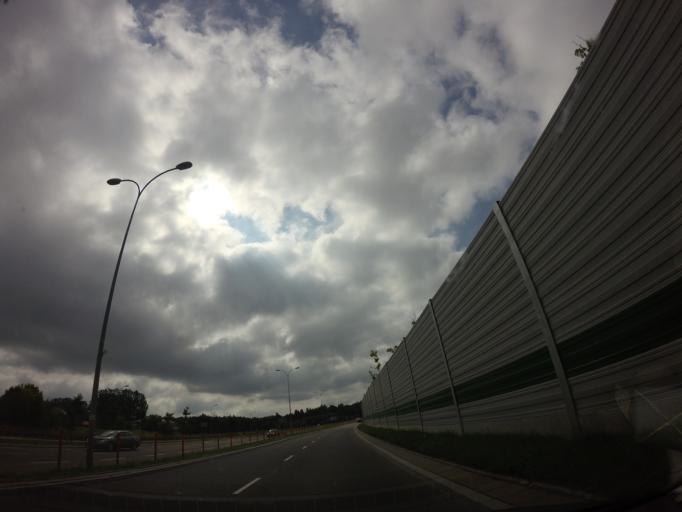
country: PL
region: Podlasie
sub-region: Bialystok
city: Bialystok
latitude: 53.1358
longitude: 23.2206
